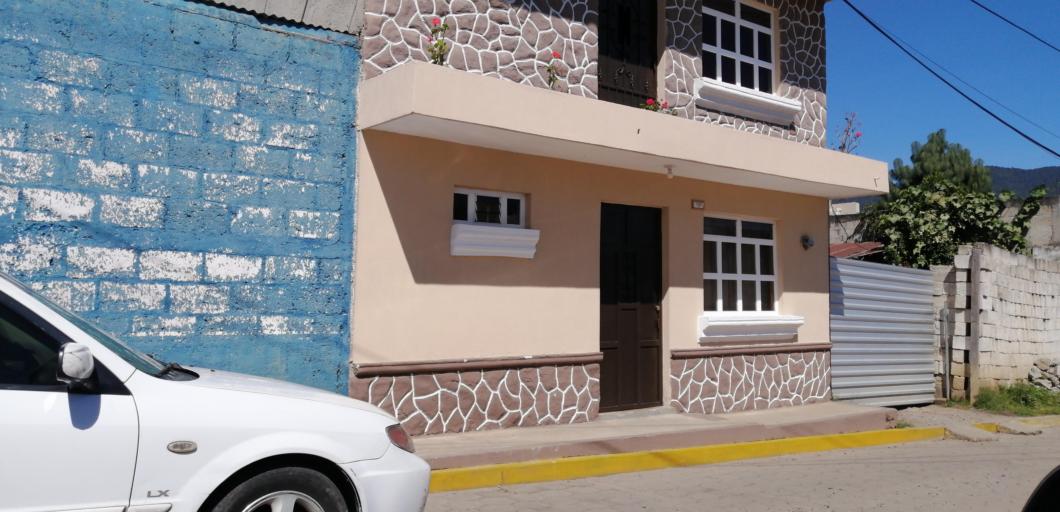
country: GT
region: Quetzaltenango
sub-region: Municipio de La Esperanza
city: La Esperanza
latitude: 14.8670
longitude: -91.5545
